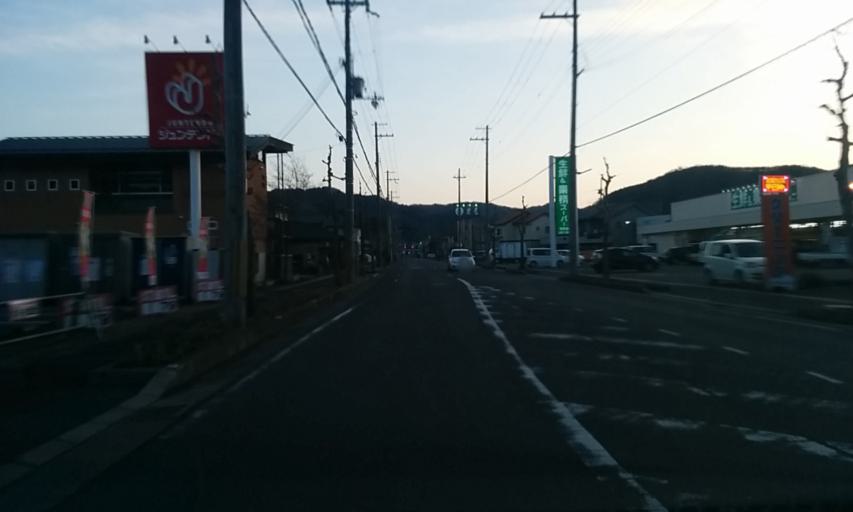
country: JP
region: Kyoto
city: Ayabe
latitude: 35.3050
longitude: 135.2623
